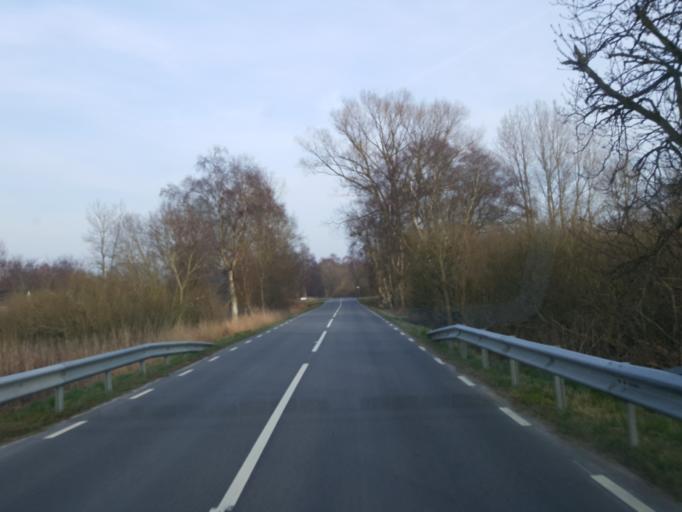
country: SE
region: Skane
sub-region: Ystads Kommun
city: Kopingebro
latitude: 55.3939
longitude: 14.1644
